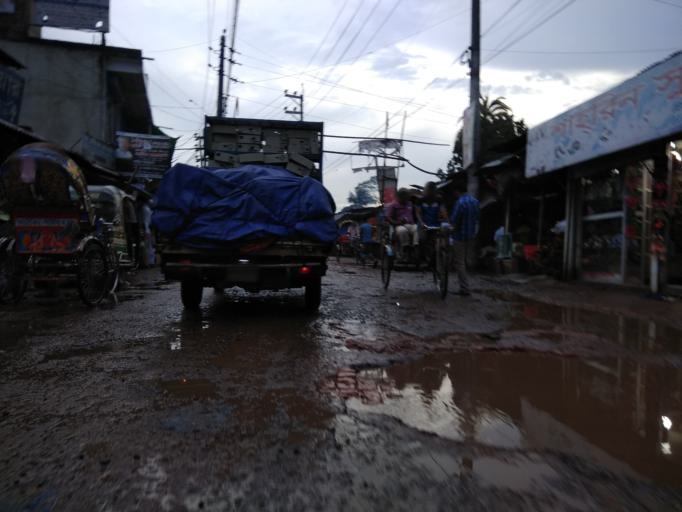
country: BD
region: Dhaka
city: Azimpur
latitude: 23.6863
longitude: 90.3082
